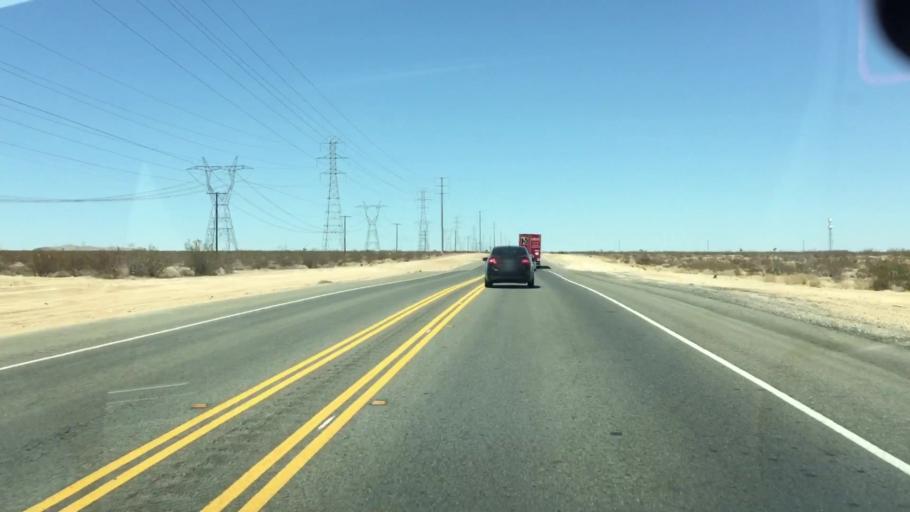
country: US
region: California
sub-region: San Bernardino County
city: Adelanto
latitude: 34.6967
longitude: -117.4522
